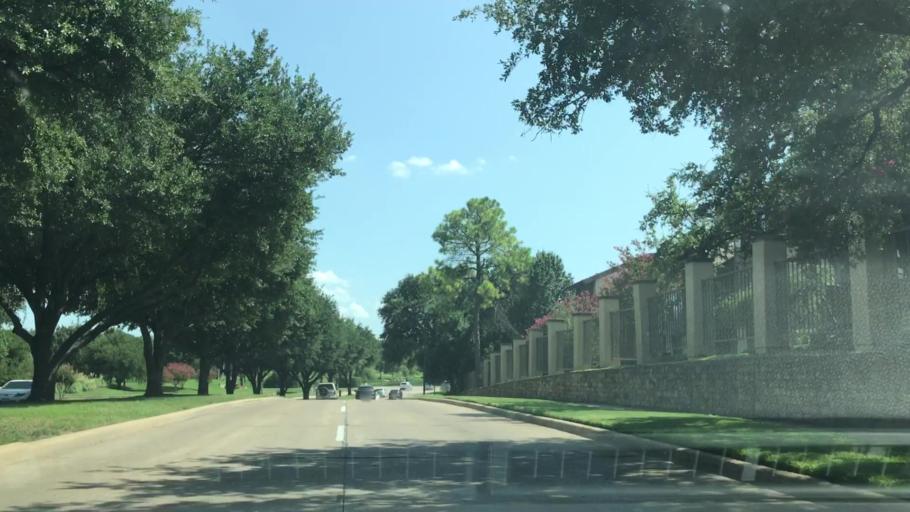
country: US
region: Texas
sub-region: Dallas County
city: Irving
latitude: 32.8608
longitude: -96.9509
